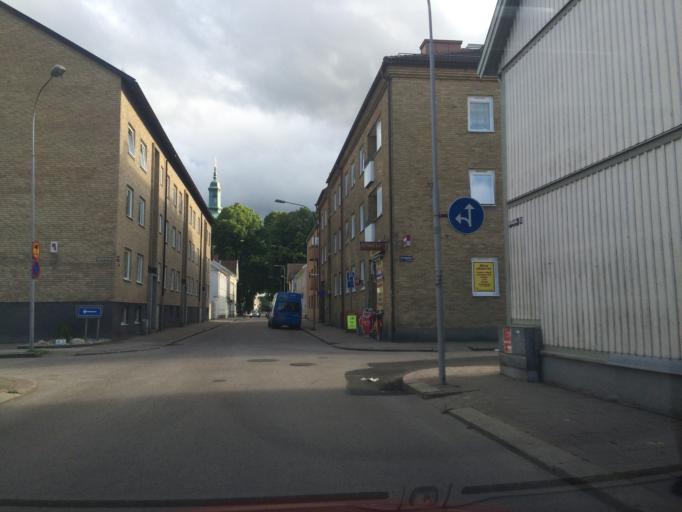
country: SE
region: Vaestra Goetaland
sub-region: Vanersborgs Kommun
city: Vanersborg
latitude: 58.3822
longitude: 12.3266
